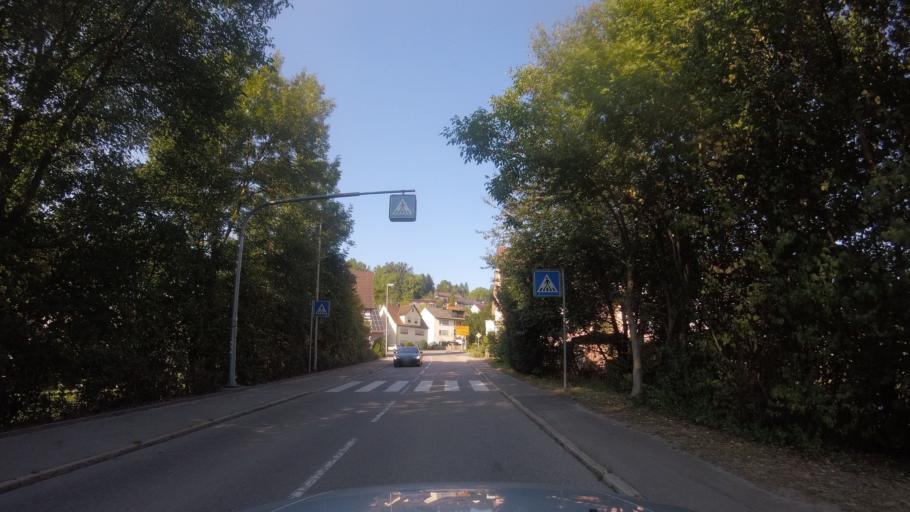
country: DE
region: Baden-Wuerttemberg
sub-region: Regierungsbezirk Stuttgart
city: Kirchberg an der Murr
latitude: 48.9410
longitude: 9.3307
